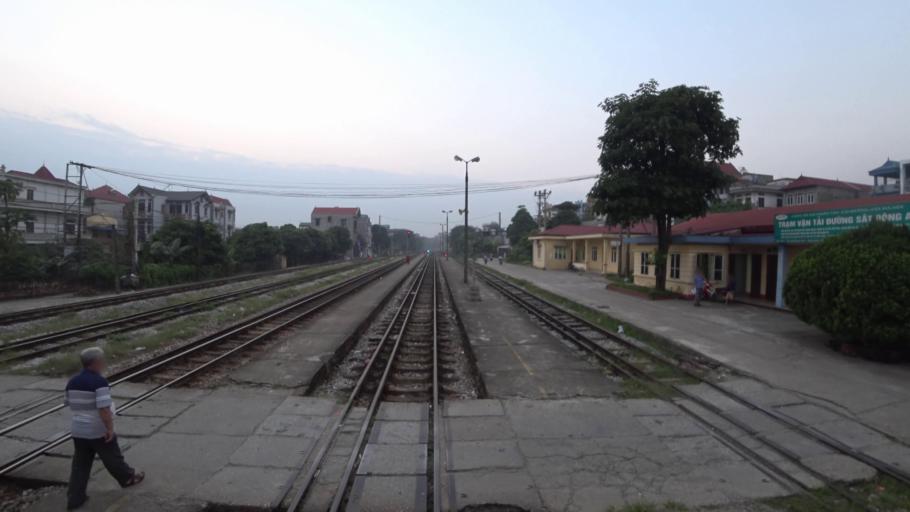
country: VN
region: Ha Noi
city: Dong Anh
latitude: 21.1958
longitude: 105.8542
